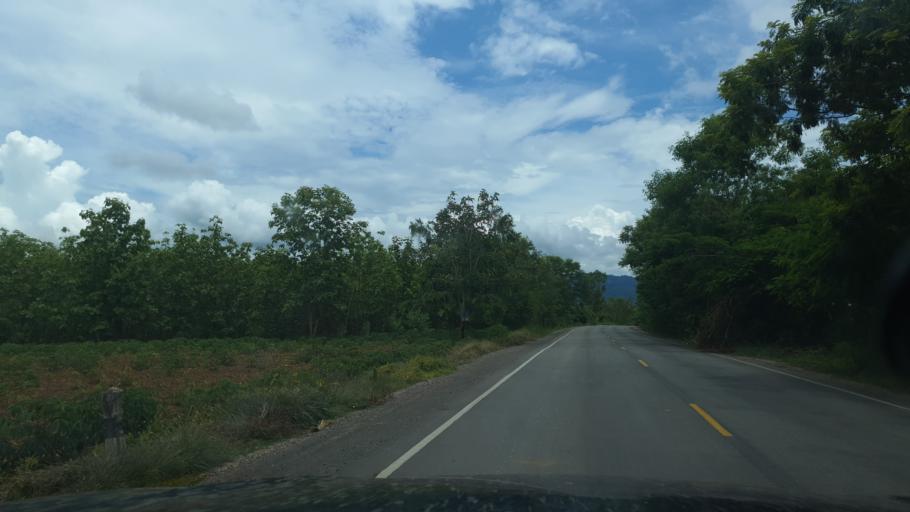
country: TH
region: Lampang
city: Sop Prap
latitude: 17.9237
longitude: 99.3823
